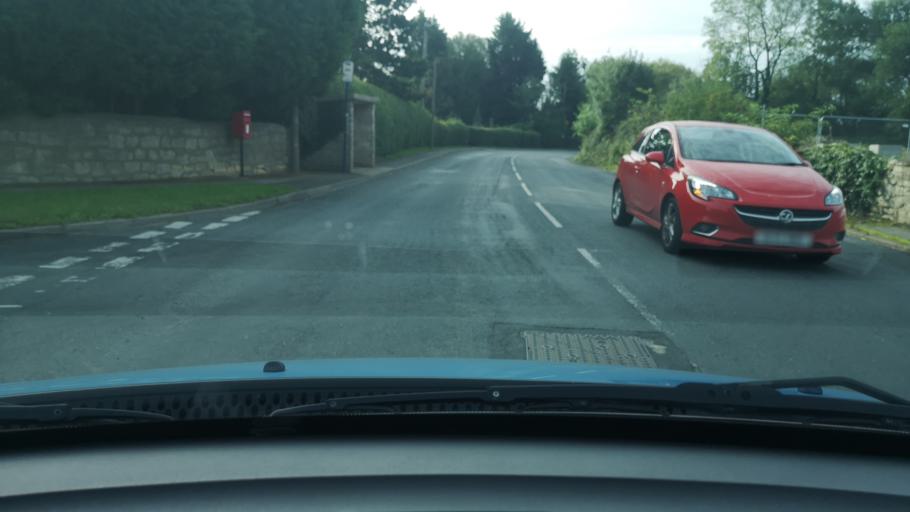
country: GB
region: England
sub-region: Doncaster
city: Campsall
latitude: 53.6047
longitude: -1.1697
